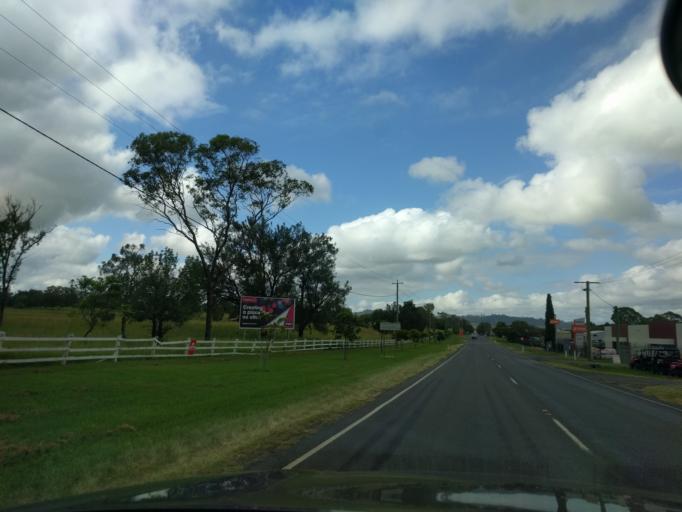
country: AU
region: Queensland
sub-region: Logan
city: Cedar Vale
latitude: -27.9956
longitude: 152.9899
